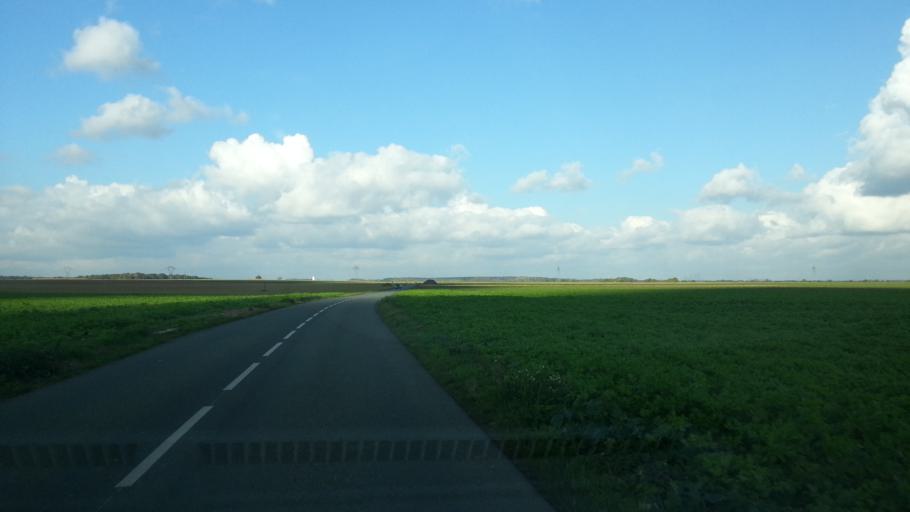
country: FR
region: Picardie
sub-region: Departement de l'Oise
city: Villers-sous-Saint-Leu
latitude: 49.2339
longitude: 2.4107
